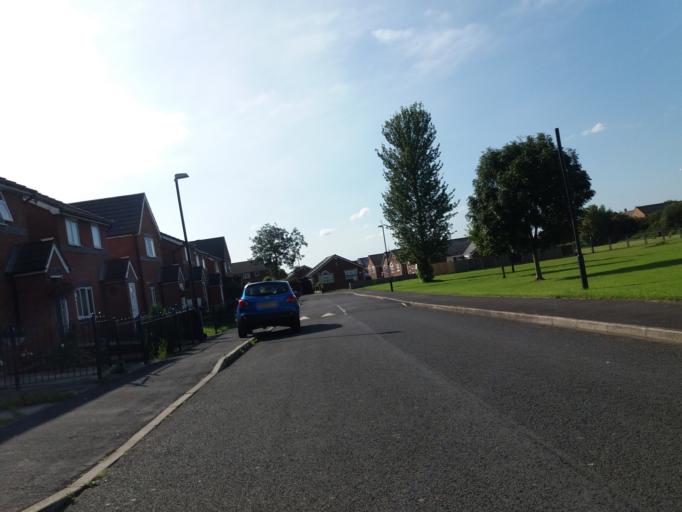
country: GB
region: England
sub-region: Lancashire
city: Coppull
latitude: 53.6428
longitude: -2.6450
